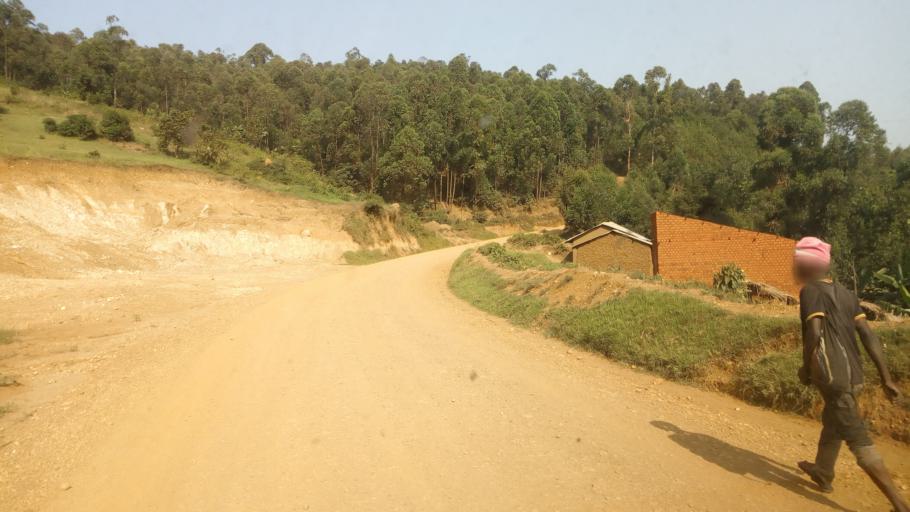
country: UG
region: Western Region
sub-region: Kanungu District
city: Ntungamo
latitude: -0.8315
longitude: 29.6960
